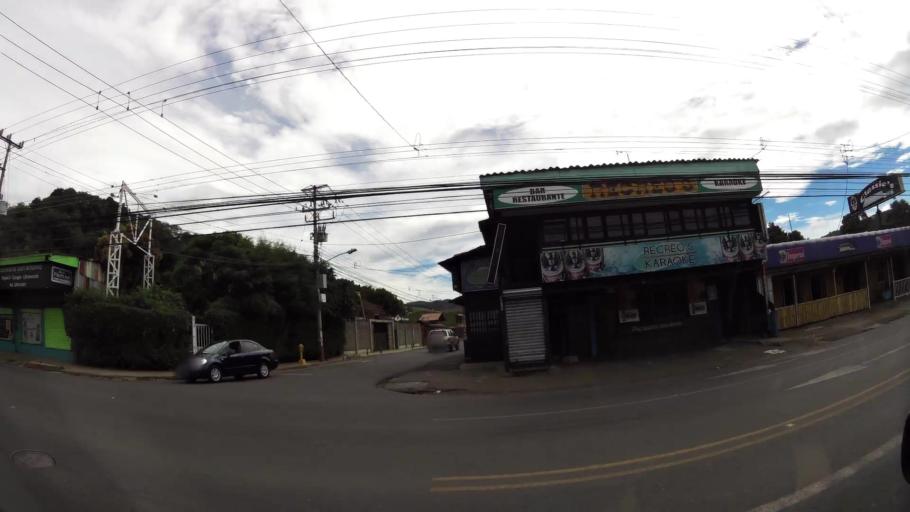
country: CR
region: San Jose
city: Curridabat
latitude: 9.9017
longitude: -84.0453
